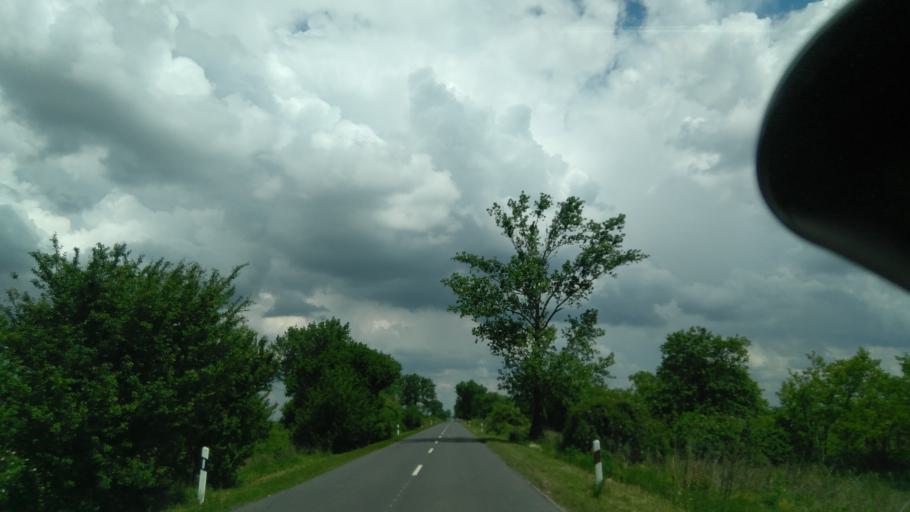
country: HU
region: Bekes
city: Devavanya
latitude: 47.0054
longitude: 20.9181
